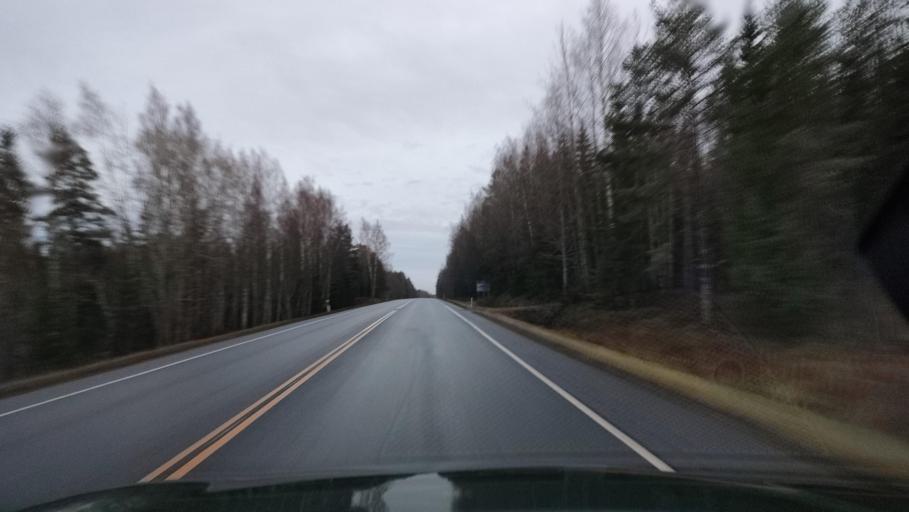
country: FI
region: Ostrobothnia
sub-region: Vaasa
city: Ristinummi
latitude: 63.0172
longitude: 21.7592
